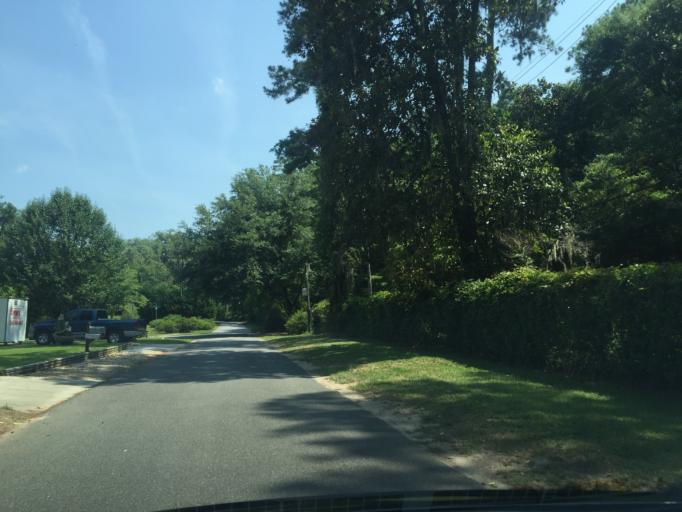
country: US
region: Georgia
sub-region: Chatham County
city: Montgomery
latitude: 31.9657
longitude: -81.1262
